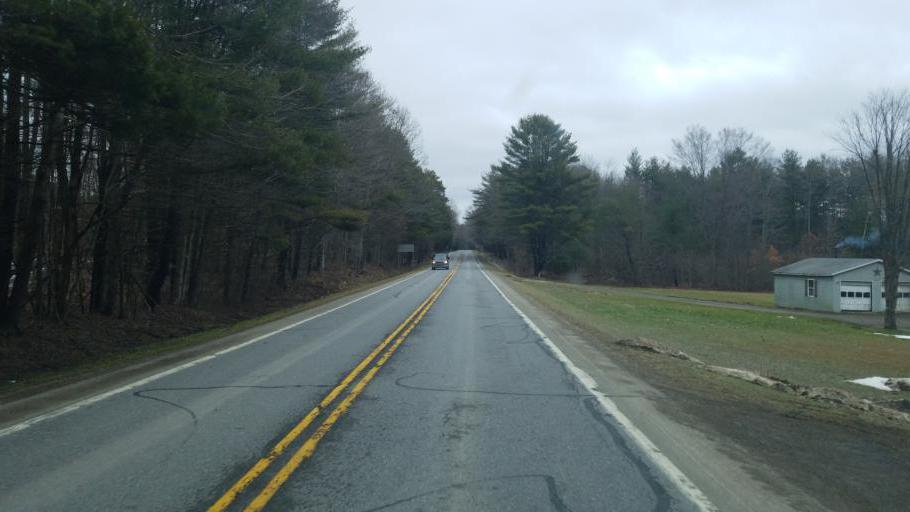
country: US
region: Pennsylvania
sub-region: Forest County
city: Marienville
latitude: 41.4124
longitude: -79.2228
